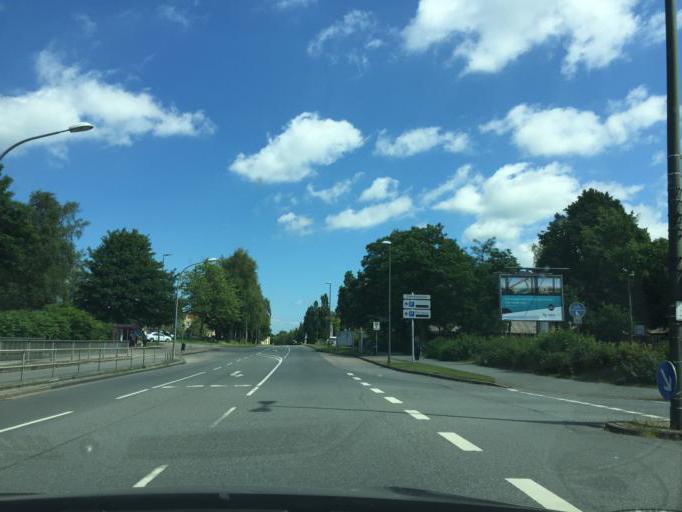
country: DE
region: Schleswig-Holstein
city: Flensburg
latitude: 54.7778
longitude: 9.4241
